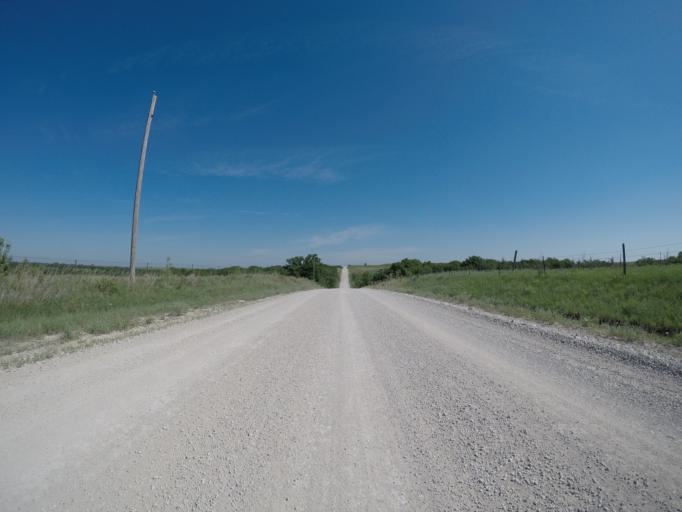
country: US
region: Kansas
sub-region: Wabaunsee County
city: Alma
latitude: 38.9708
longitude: -96.1140
